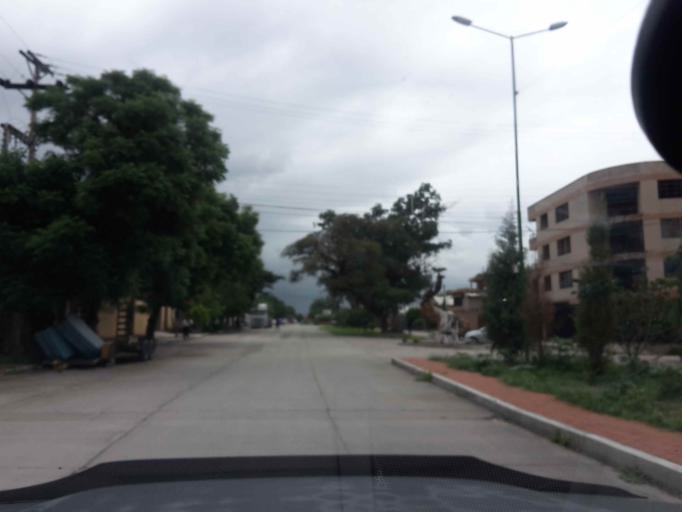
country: BO
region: Cochabamba
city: Cochabamba
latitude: -17.3767
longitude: -66.1210
